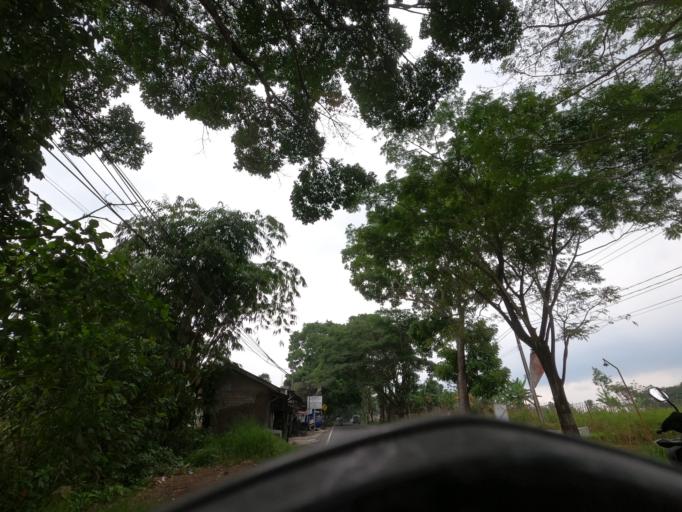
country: ID
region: West Java
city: Sukabumi
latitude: -6.7885
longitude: 107.0659
